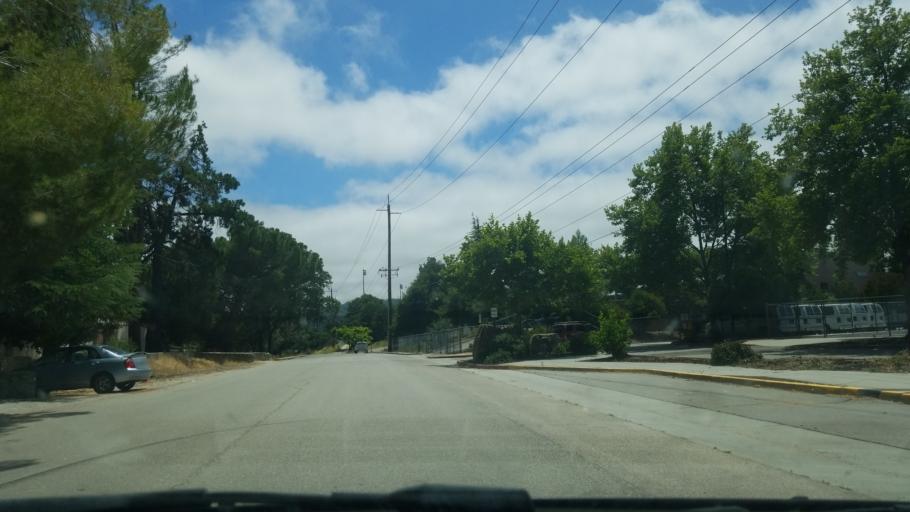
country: US
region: California
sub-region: San Luis Obispo County
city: Templeton
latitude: 35.5419
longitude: -120.7105
